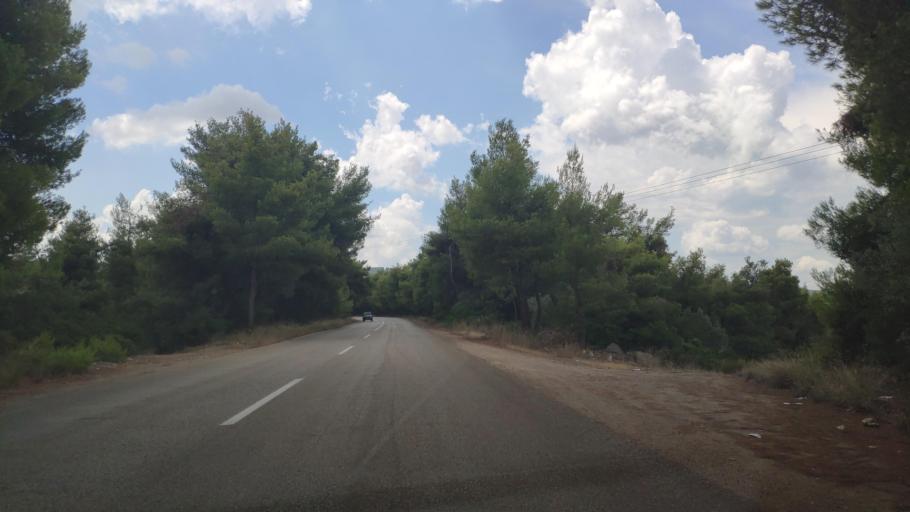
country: GR
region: Central Greece
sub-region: Nomos Fthiotidos
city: Malesina
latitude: 38.6237
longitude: 23.1804
